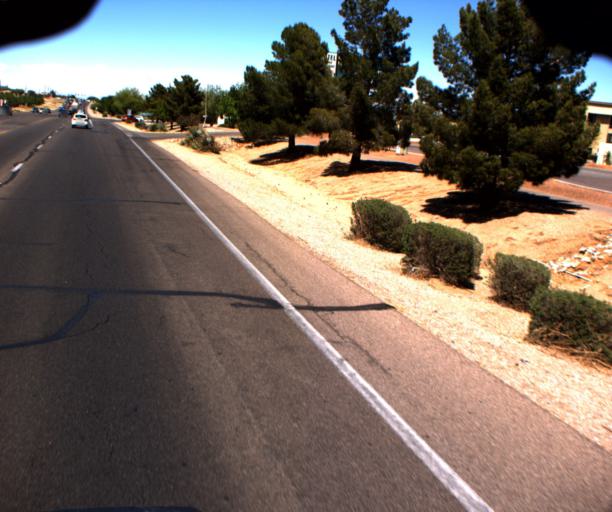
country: US
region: Arizona
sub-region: Cochise County
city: Sierra Vista
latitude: 31.5388
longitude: -110.2573
